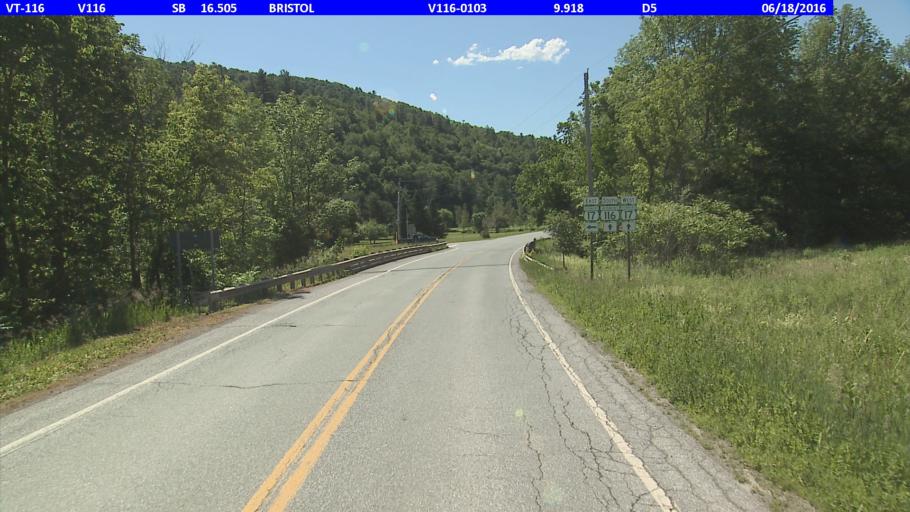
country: US
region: Vermont
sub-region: Addison County
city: Bristol
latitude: 44.1538
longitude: -73.0459
